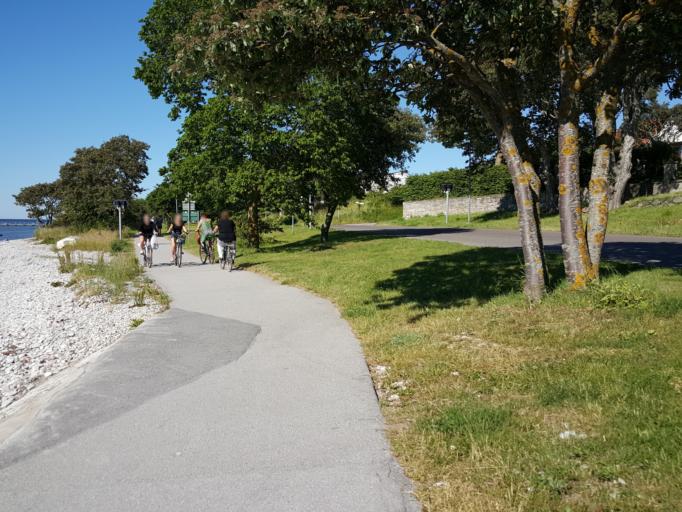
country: SE
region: Gotland
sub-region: Gotland
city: Visby
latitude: 57.6505
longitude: 18.3010
